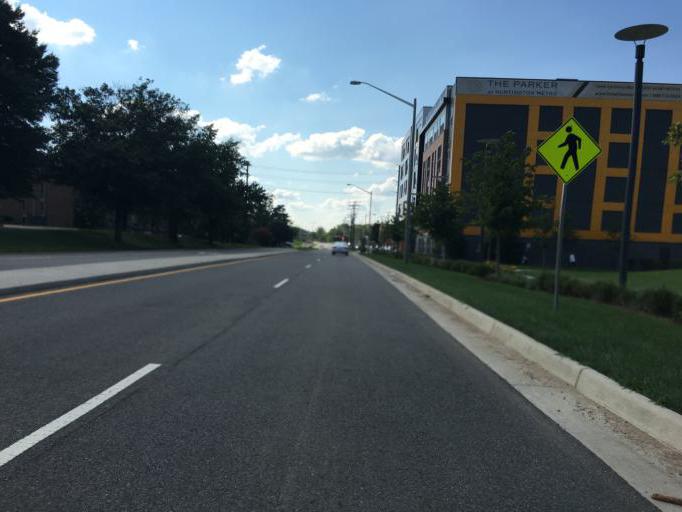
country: US
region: Virginia
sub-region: Fairfax County
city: Huntington
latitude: 38.7966
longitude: -77.0757
